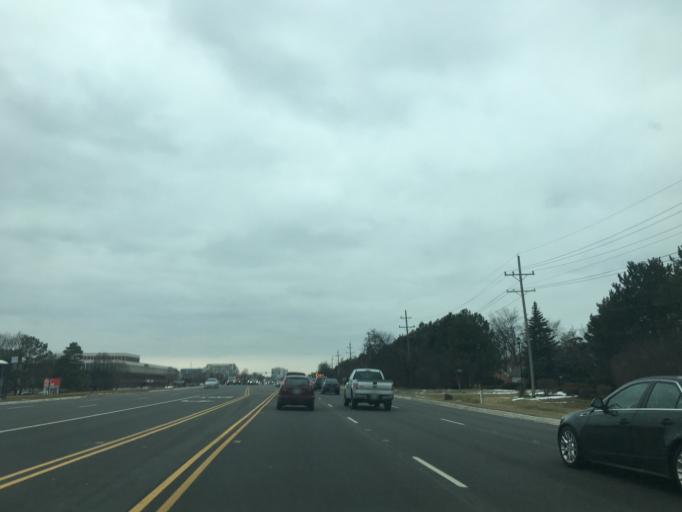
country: US
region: Illinois
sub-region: DuPage County
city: Oakbrook Terrace
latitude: 41.8447
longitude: -87.9868
